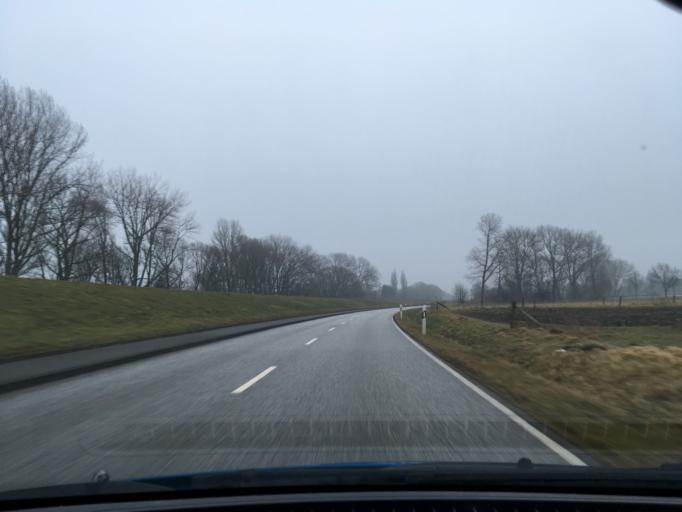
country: DE
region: Hamburg
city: Harburg
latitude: 53.4717
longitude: 10.0302
